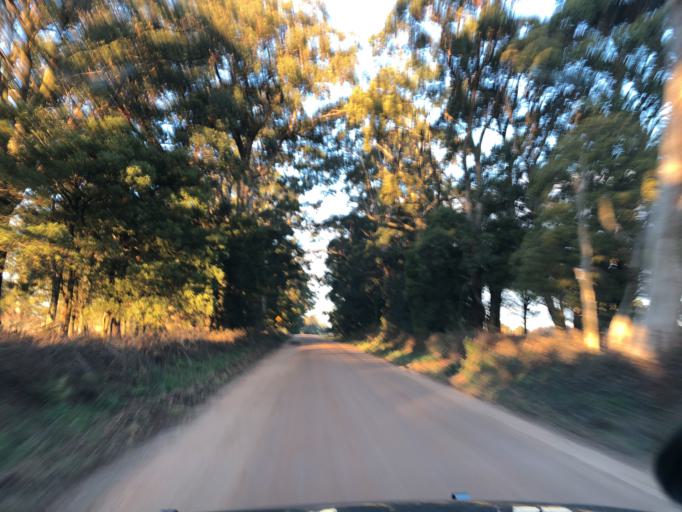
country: AU
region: Victoria
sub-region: Moorabool
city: Bacchus Marsh
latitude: -37.4063
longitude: 144.3645
